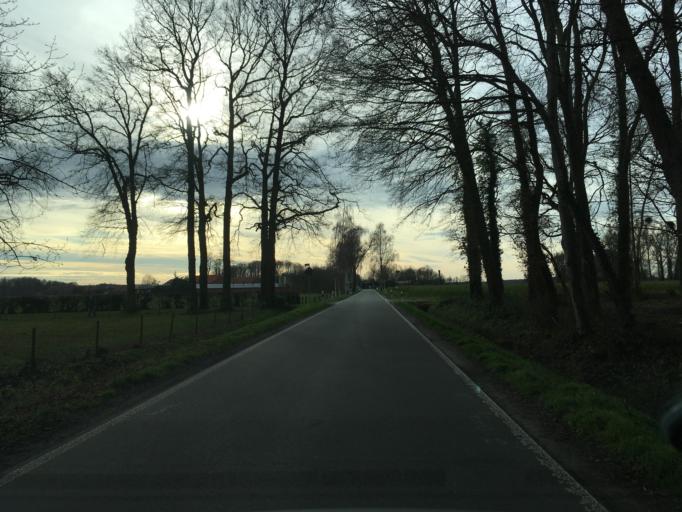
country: DE
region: North Rhine-Westphalia
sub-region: Regierungsbezirk Munster
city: Legden
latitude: 52.0712
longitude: 7.0998
